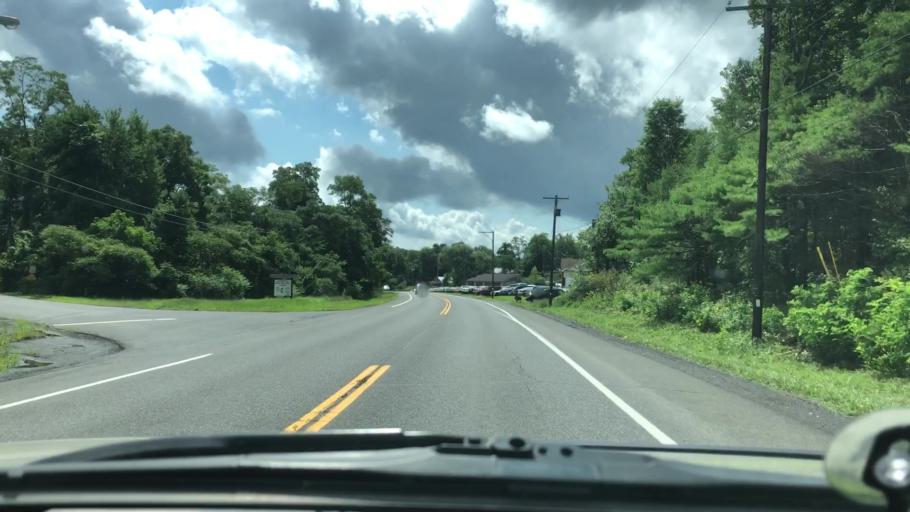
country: US
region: New York
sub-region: Ulster County
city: Manorville
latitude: 42.1236
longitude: -73.9947
